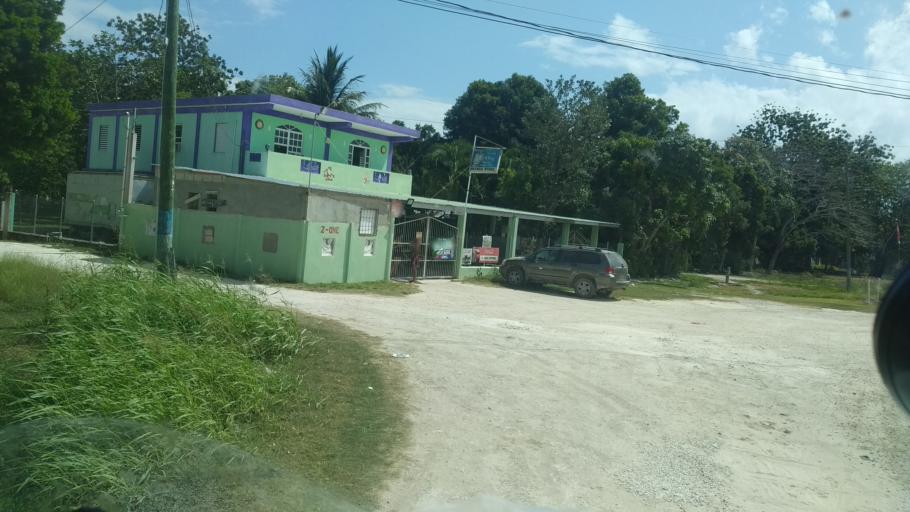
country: BZ
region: Corozal
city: Corozal
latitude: 18.3903
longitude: -88.4152
